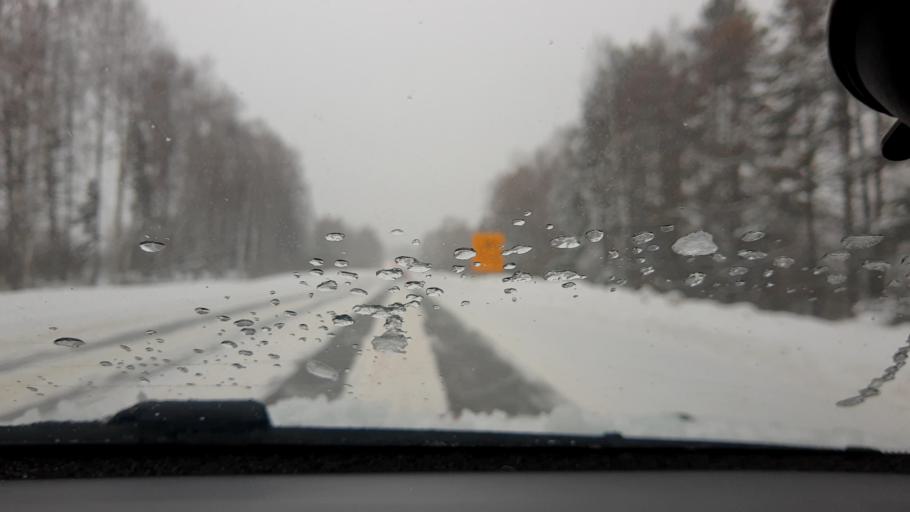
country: RU
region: Nizjnij Novgorod
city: Purekh
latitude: 56.6331
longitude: 43.1602
